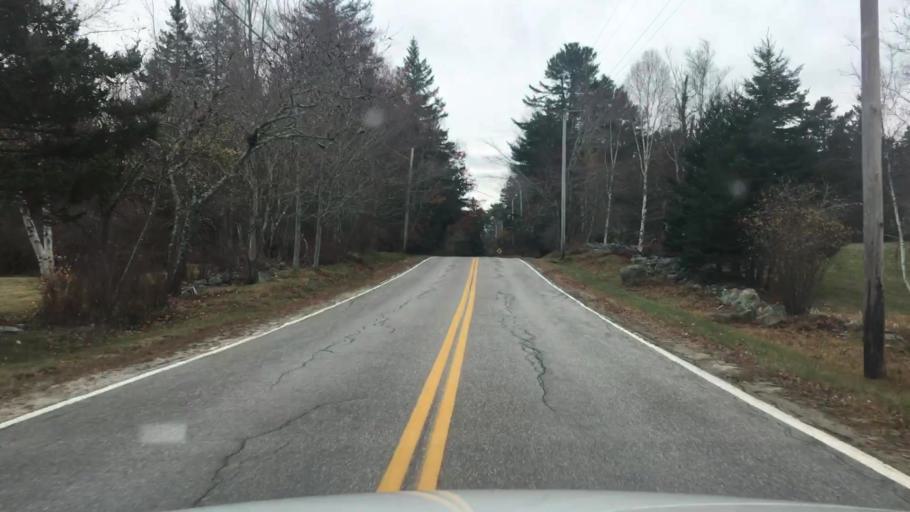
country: US
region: Maine
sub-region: Hancock County
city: Sedgwick
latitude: 44.2936
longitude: -68.5554
